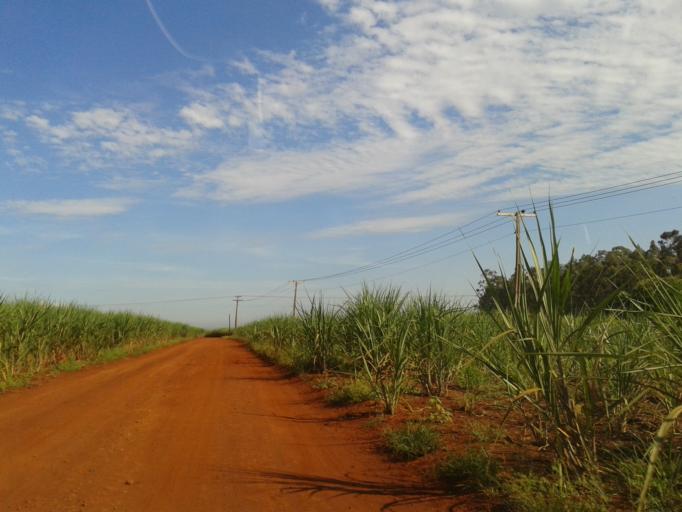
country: BR
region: Minas Gerais
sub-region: Centralina
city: Centralina
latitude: -18.6470
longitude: -49.2425
